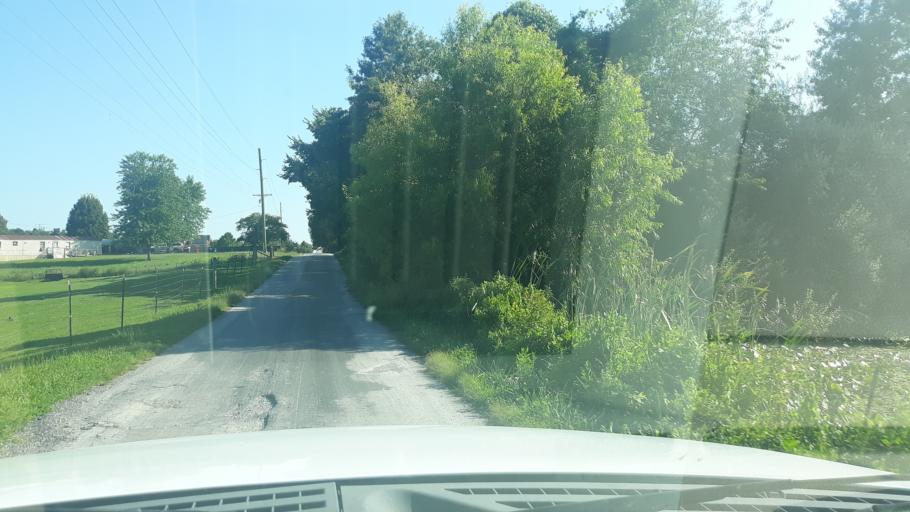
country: US
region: Illinois
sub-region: Saline County
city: Harrisburg
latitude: 37.8606
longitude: -88.5963
